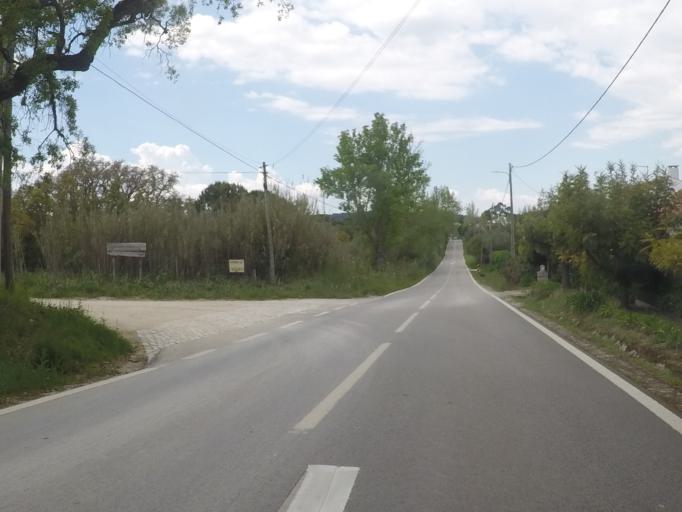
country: PT
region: Setubal
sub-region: Sesimbra
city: Sesimbra
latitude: 38.4757
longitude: -9.0298
